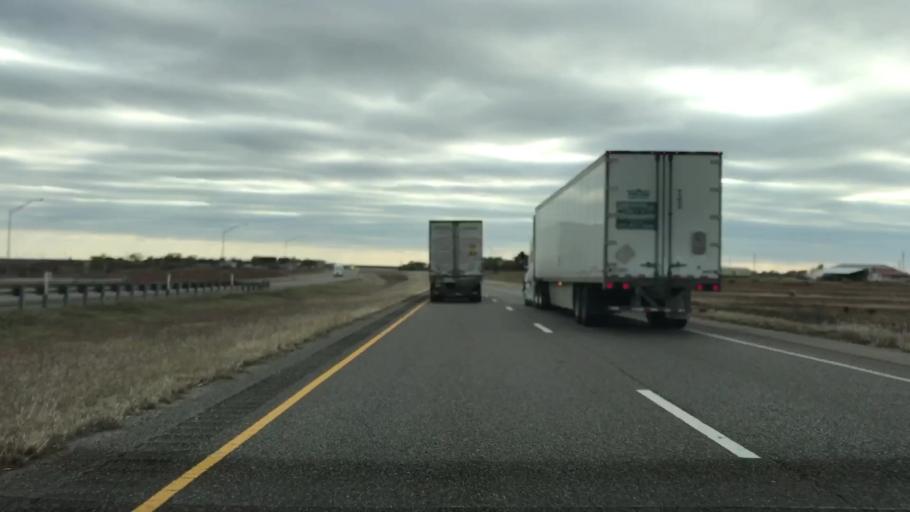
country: US
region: Oklahoma
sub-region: Beckham County
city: Sayre
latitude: 35.3147
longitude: -99.6130
